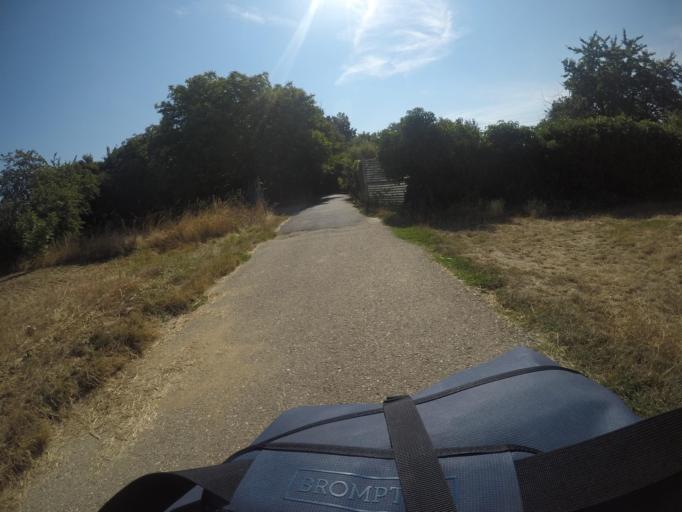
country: DE
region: Hesse
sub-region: Regierungsbezirk Darmstadt
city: Hattersheim
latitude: 50.0883
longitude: 8.4970
